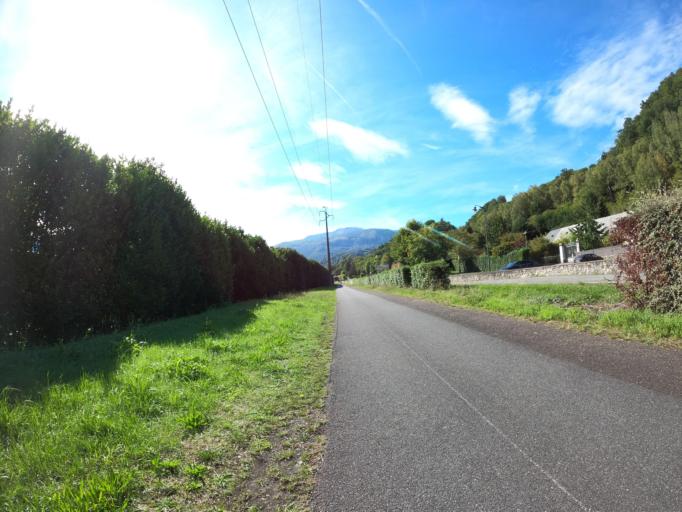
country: FR
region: Midi-Pyrenees
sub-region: Departement des Hautes-Pyrenees
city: Argeles-Gazost
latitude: 43.0158
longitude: -0.0973
